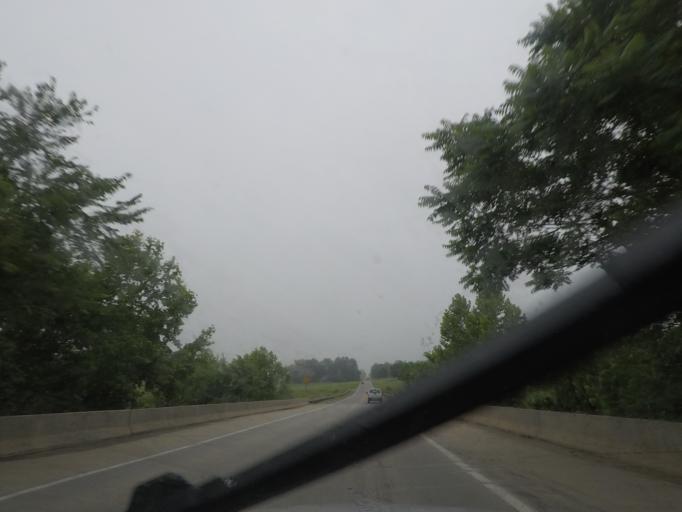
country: US
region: Virginia
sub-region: Prince Edward County
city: Farmville
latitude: 37.3404
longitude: -78.4714
